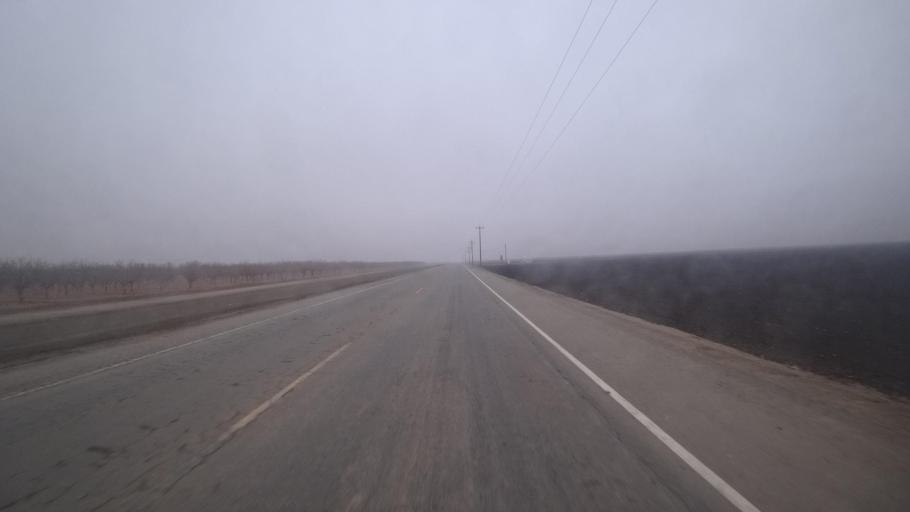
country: US
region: California
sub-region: Kern County
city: Buttonwillow
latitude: 35.4150
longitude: -119.5185
